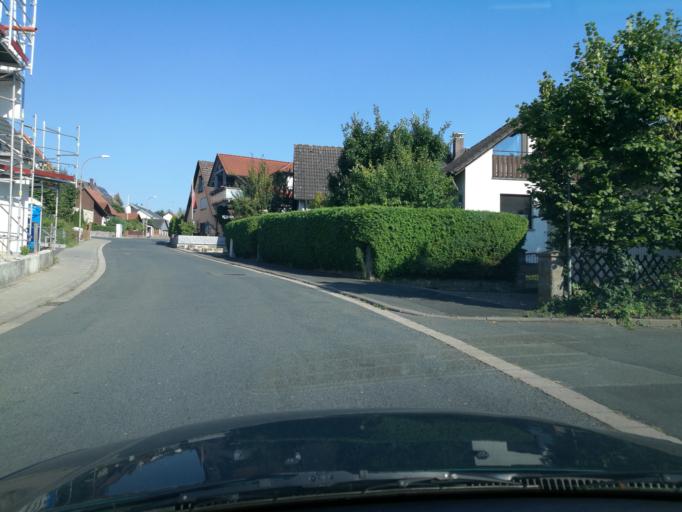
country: DE
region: Bavaria
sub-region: Regierungsbezirk Mittelfranken
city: Rottenbach
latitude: 49.6638
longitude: 10.9245
